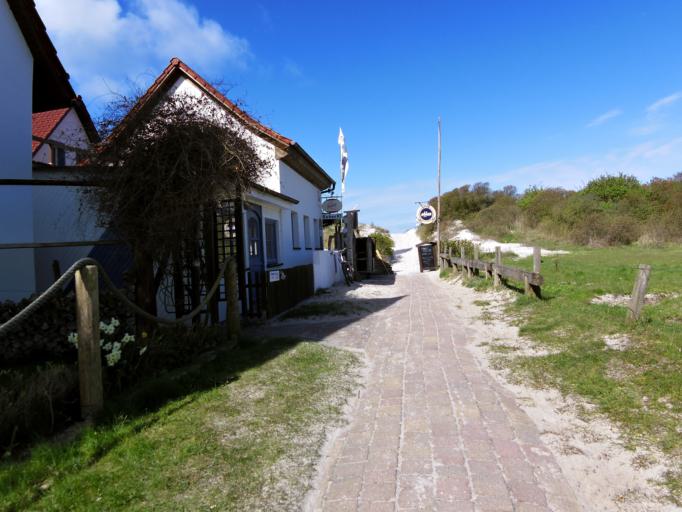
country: DE
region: Mecklenburg-Vorpommern
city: Hiddensee
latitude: 54.5722
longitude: 13.1030
